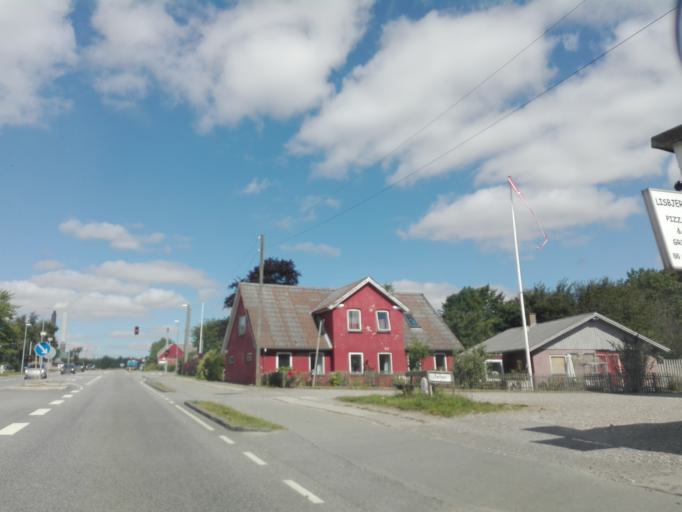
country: DK
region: Central Jutland
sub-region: Arhus Kommune
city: Trige
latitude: 56.2214
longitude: 10.1648
